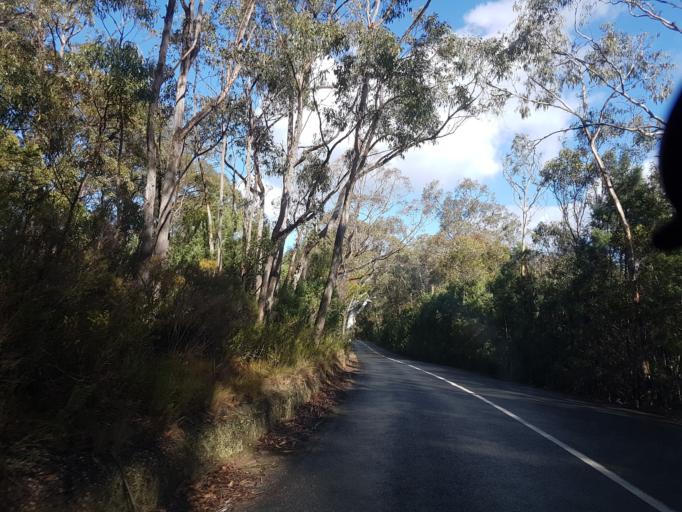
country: AU
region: South Australia
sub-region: Adelaide Hills
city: Heathfield
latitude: -35.0366
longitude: 138.7083
